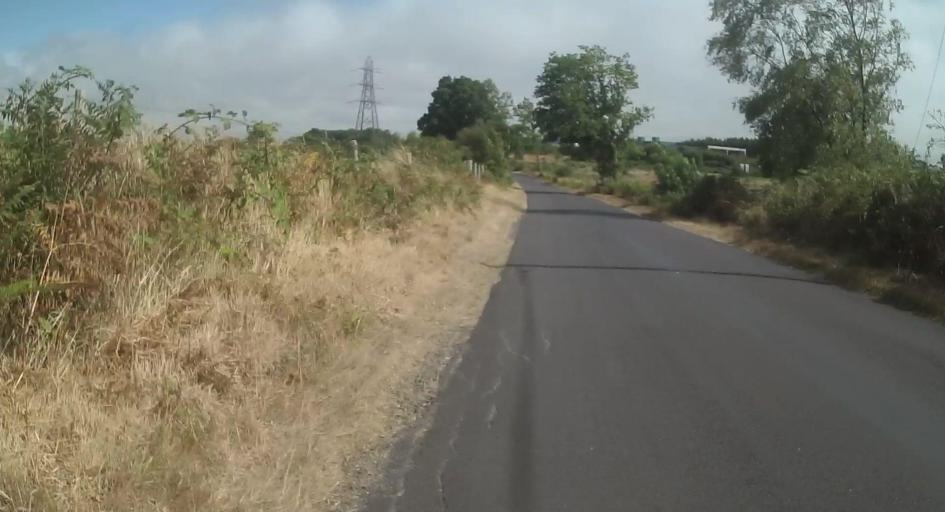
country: GB
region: England
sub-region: Dorset
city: Bovington Camp
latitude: 50.6887
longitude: -2.2657
